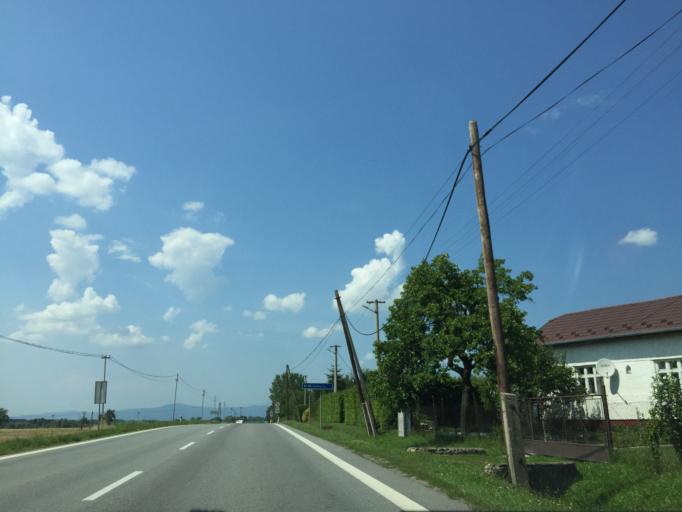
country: UA
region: Zakarpattia
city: Storozhnytsya
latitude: 48.6849
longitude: 22.2424
